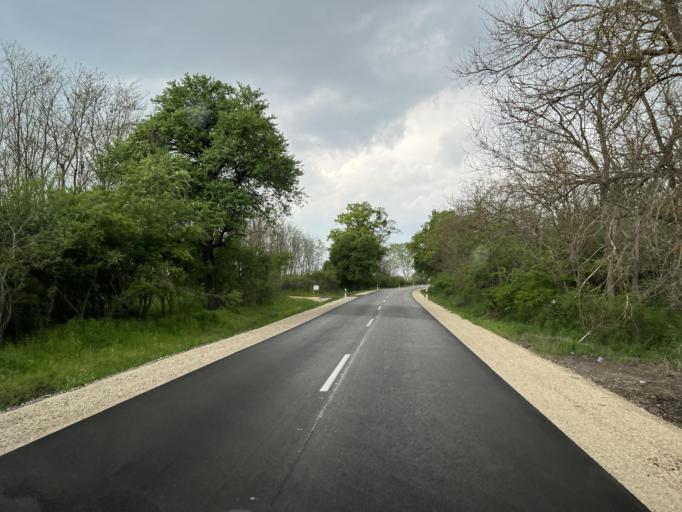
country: HU
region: Pest
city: Csemo
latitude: 47.0673
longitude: 19.6976
